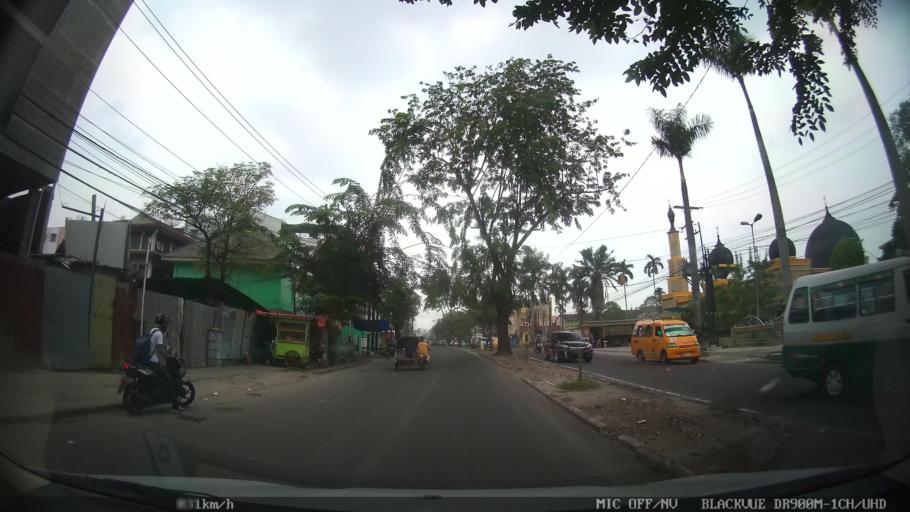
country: ID
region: North Sumatra
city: Medan
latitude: 3.5710
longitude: 98.6862
